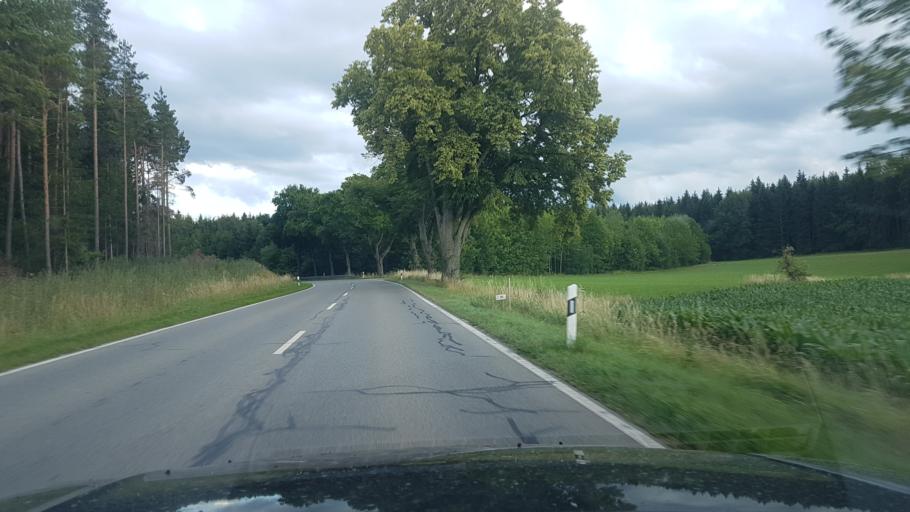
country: DE
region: Baden-Wuerttemberg
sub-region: Freiburg Region
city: Braunlingen
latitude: 47.9629
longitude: 8.4460
